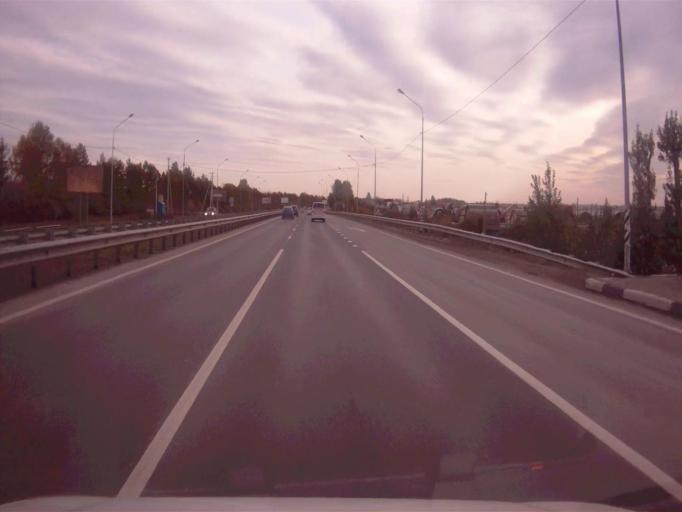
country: RU
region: Chelyabinsk
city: Novosineglazovskiy
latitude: 55.0312
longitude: 61.4459
